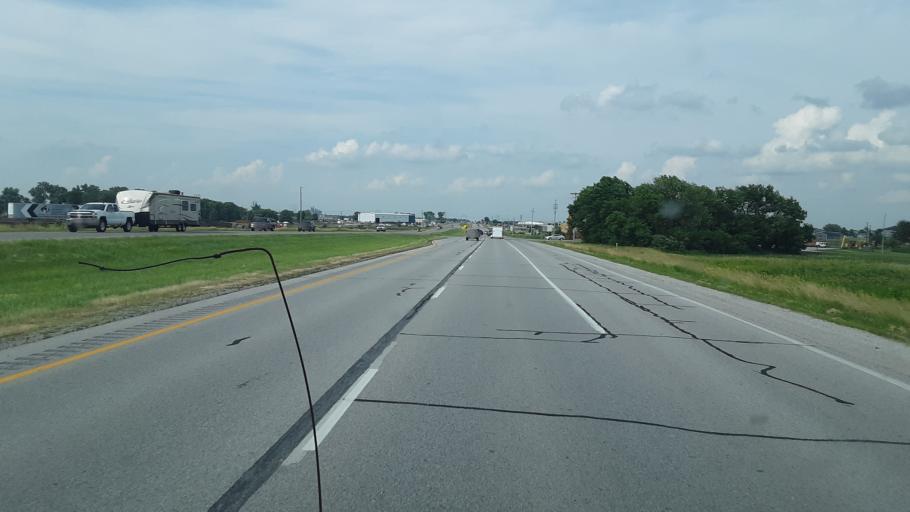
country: US
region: Iowa
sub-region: Polk County
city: Altoona
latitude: 41.6685
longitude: -93.4861
